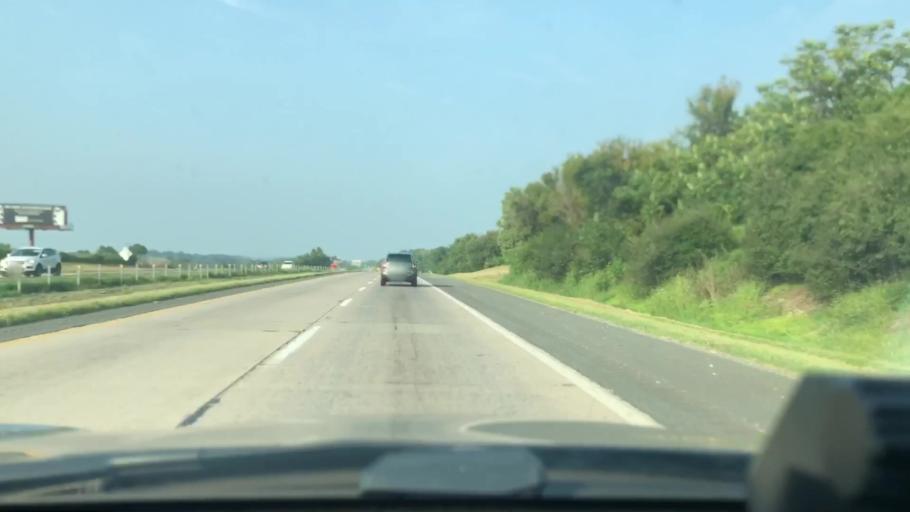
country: US
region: Pennsylvania
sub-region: Berks County
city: Temple
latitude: 40.4195
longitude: -75.9260
